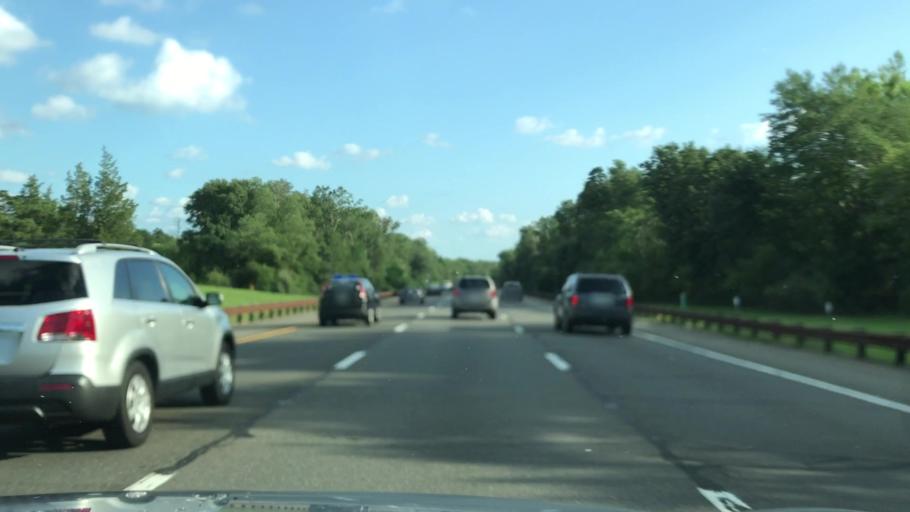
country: US
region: New Jersey
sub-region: Ocean County
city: South Toms River
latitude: 39.8889
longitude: -74.2129
